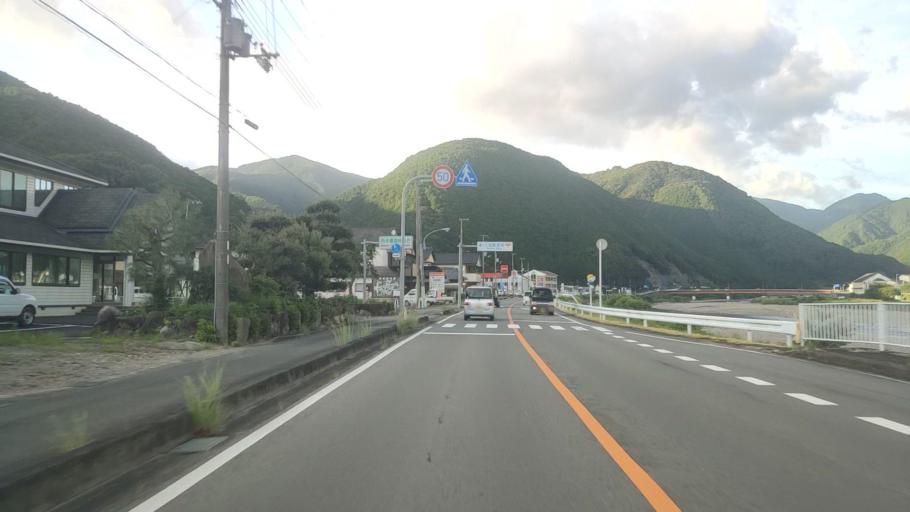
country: JP
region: Wakayama
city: Tanabe
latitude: 33.7269
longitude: 135.4828
